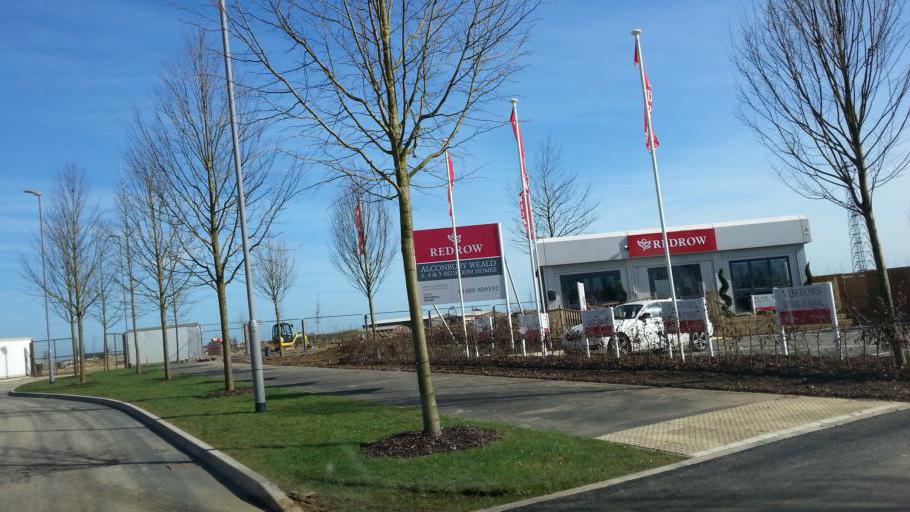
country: GB
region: England
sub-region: Cambridgeshire
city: Great Stukeley
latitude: 52.3710
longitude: -0.2305
